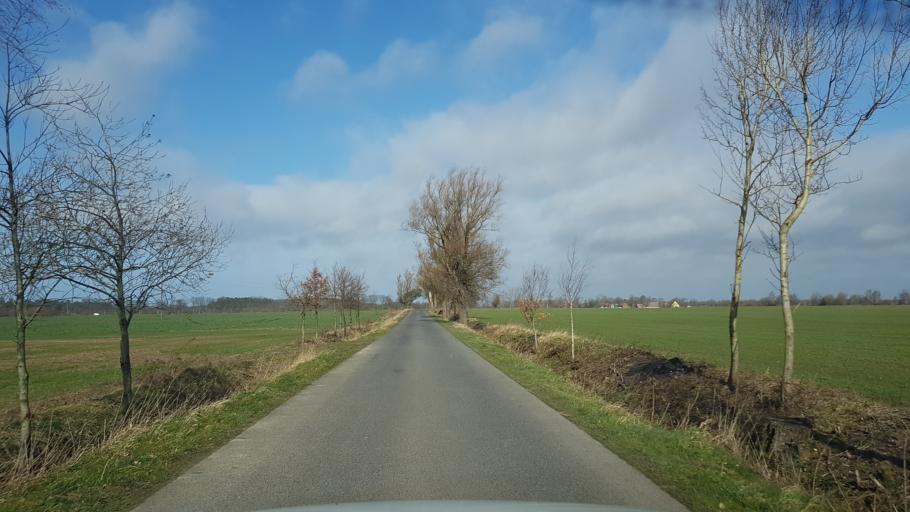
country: PL
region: West Pomeranian Voivodeship
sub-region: Powiat slawienski
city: Slawno
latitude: 54.5015
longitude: 16.6524
